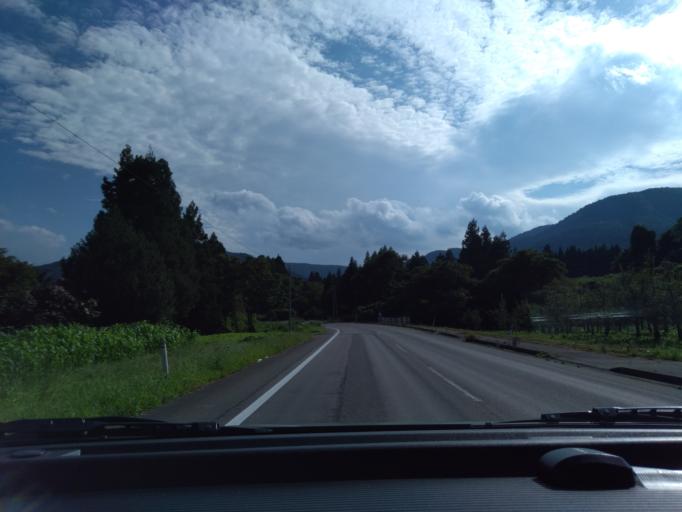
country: JP
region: Iwate
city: Morioka-shi
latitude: 39.5694
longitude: 141.0835
